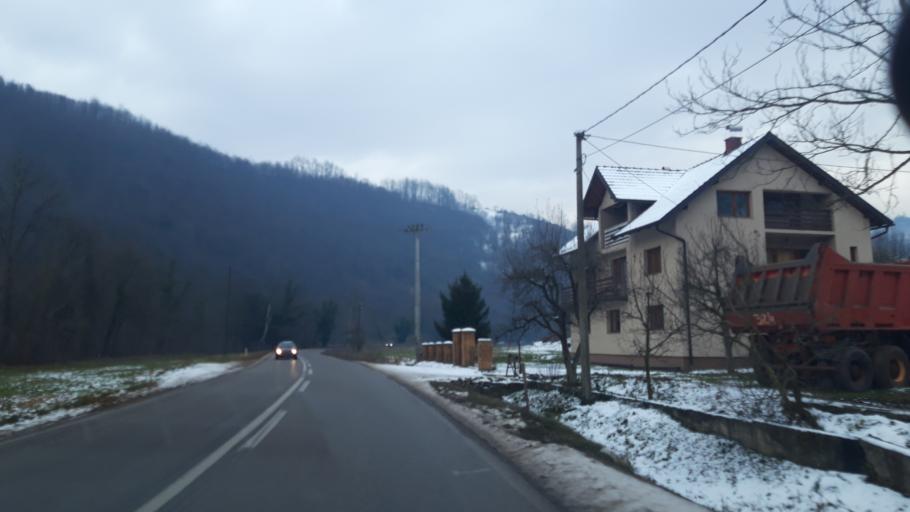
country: BA
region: Republika Srpska
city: Milici
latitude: 44.1876
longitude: 19.0725
